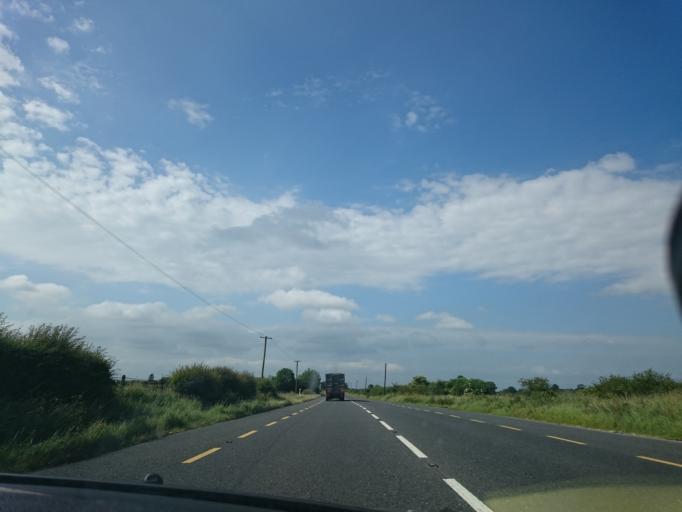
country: IE
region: Leinster
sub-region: Kilkenny
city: Kilkenny
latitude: 52.6079
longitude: -7.2434
